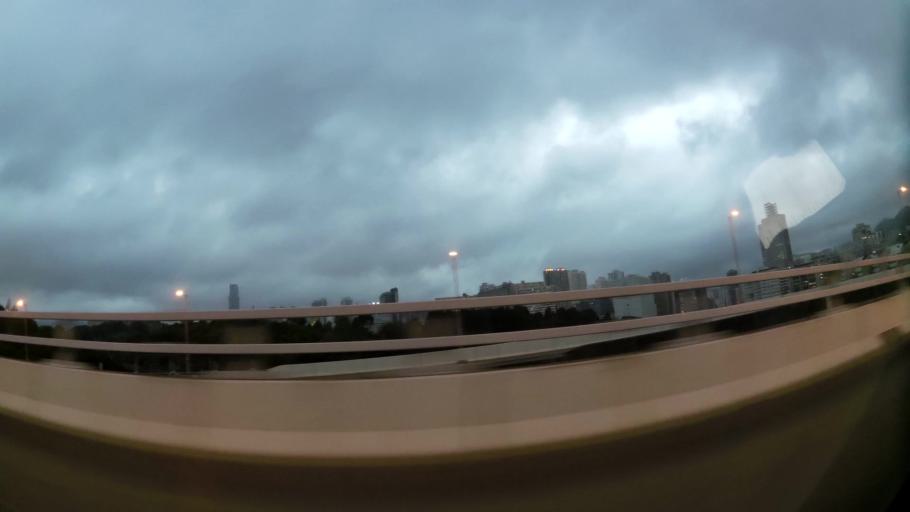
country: HK
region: Tsuen Wan
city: Tsuen Wan
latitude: 22.3526
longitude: 114.1209
